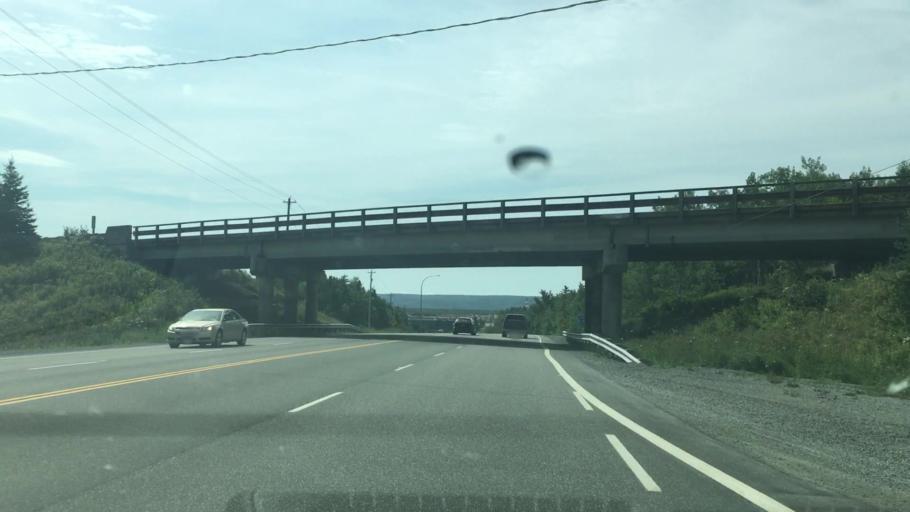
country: CA
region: Nova Scotia
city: Port Hawkesbury
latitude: 45.6255
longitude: -61.3325
